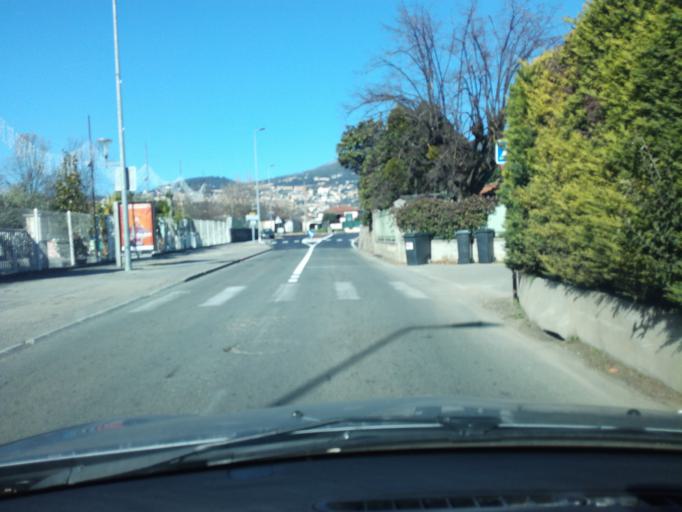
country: FR
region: Provence-Alpes-Cote d'Azur
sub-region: Departement des Alpes-Maritimes
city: Mouans-Sartoux
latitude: 43.6438
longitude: 6.9552
